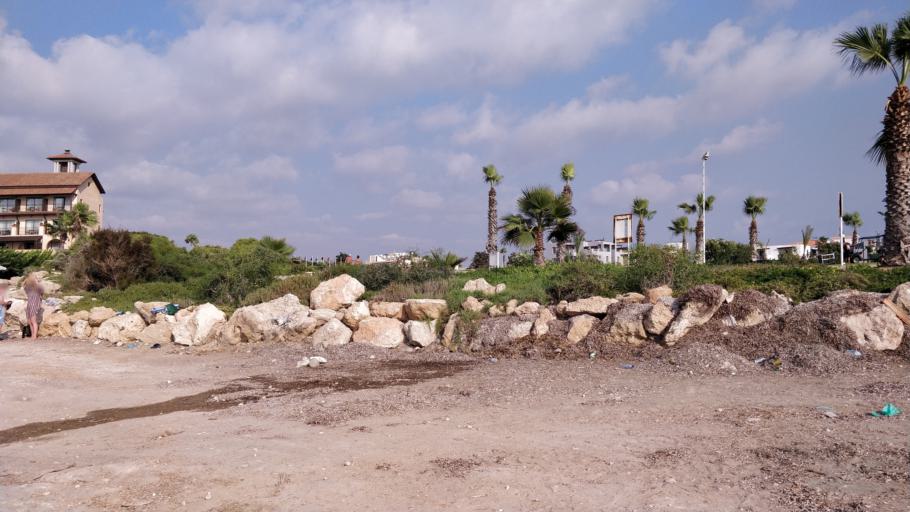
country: CY
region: Pafos
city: Paphos
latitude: 34.7716
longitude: 32.4042
